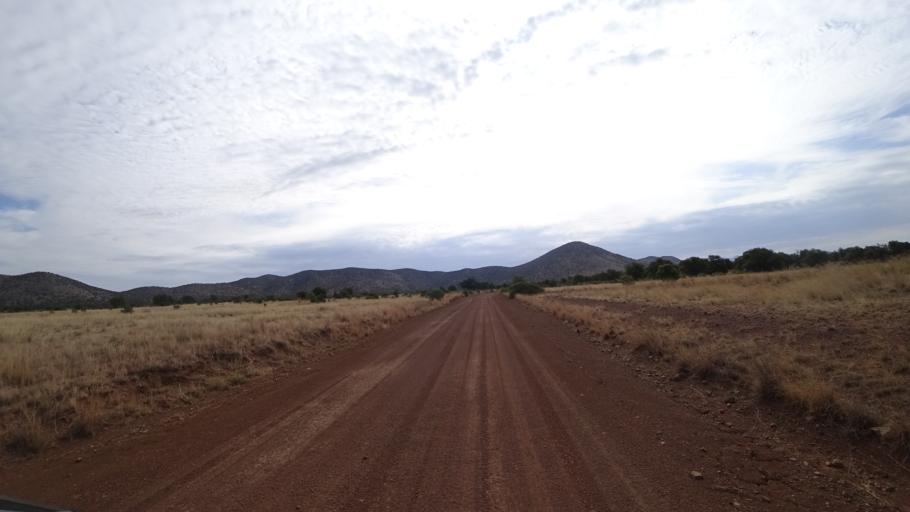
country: MX
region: Sonora
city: Santa Cruz
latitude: 31.4819
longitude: -110.5679
